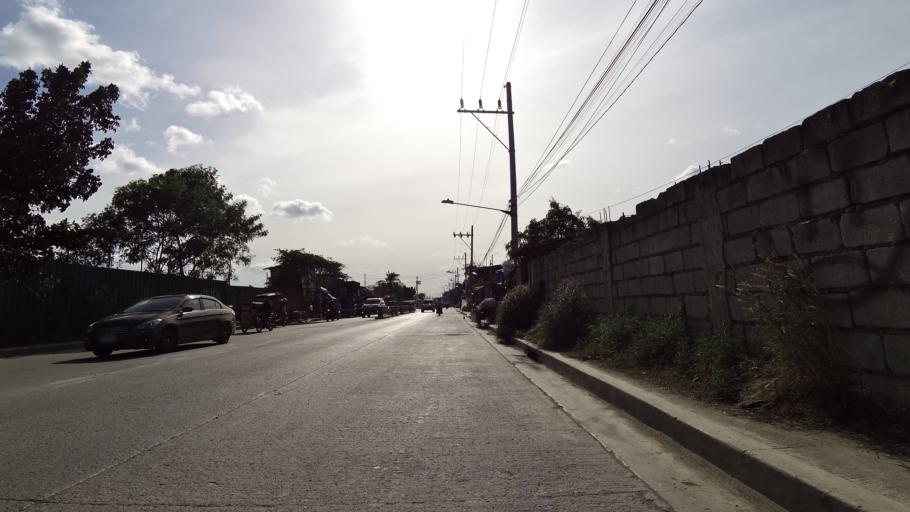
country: PH
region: Calabarzon
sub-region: Province of Rizal
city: Taytay
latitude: 14.5519
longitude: 121.1240
